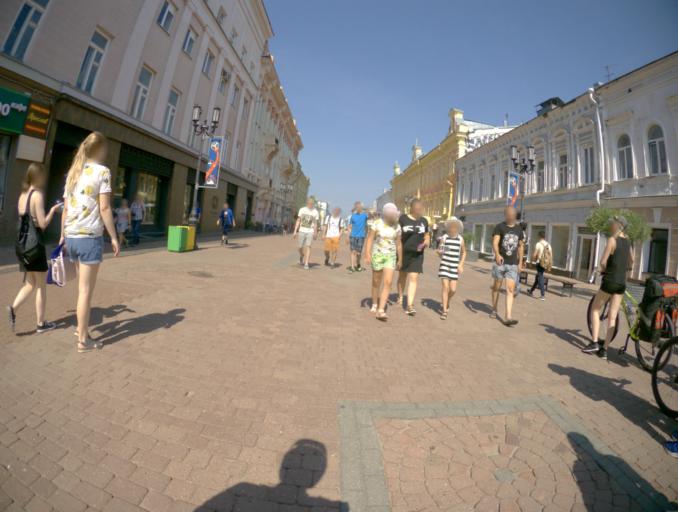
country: RU
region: Nizjnij Novgorod
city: Nizhniy Novgorod
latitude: 56.3208
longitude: 43.9991
